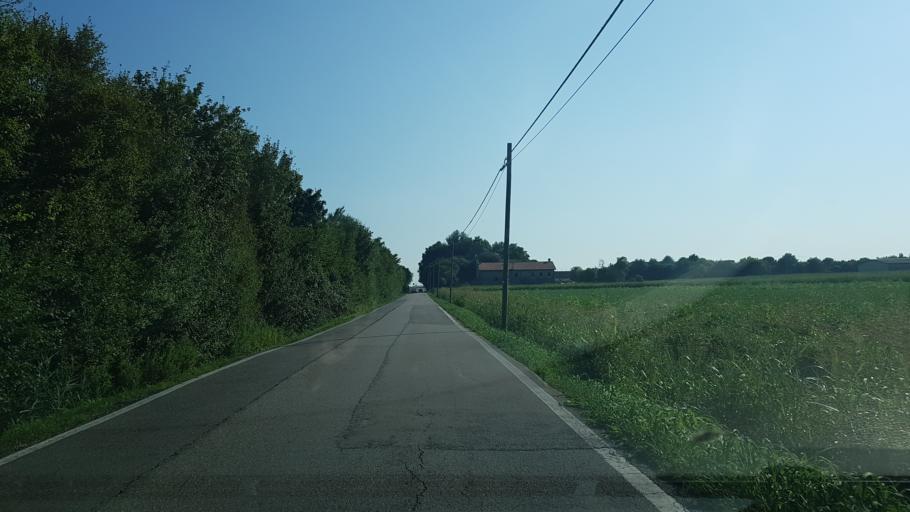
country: IT
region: Veneto
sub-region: Provincia di Venezia
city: San Giorgio di Livenza
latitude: 45.6318
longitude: 12.7829
